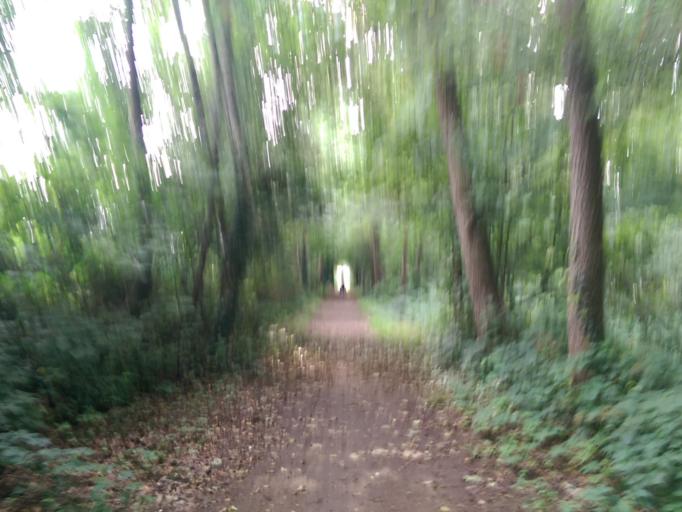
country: DE
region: North Rhine-Westphalia
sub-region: Regierungsbezirk Detmold
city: Harsewinkel
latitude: 51.9516
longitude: 8.2888
